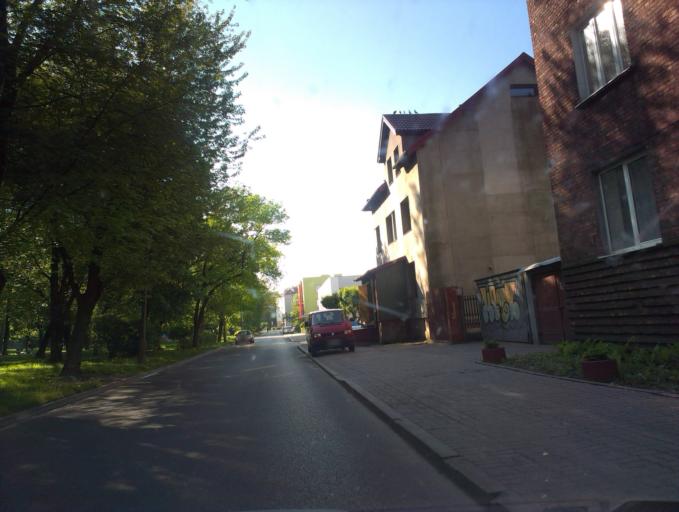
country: PL
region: Masovian Voivodeship
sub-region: Radom
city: Radom
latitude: 51.3943
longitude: 21.1470
